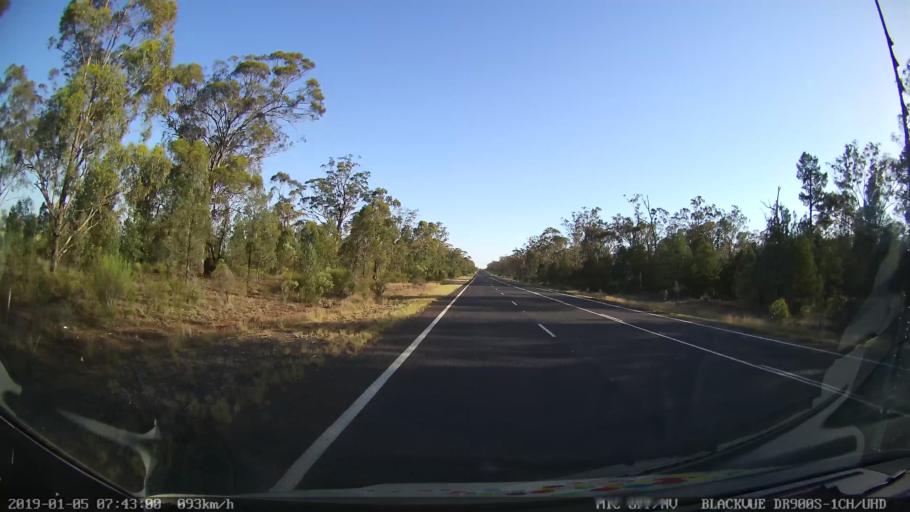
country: AU
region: New South Wales
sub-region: Gilgandra
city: Gilgandra
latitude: -31.8906
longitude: 148.6309
